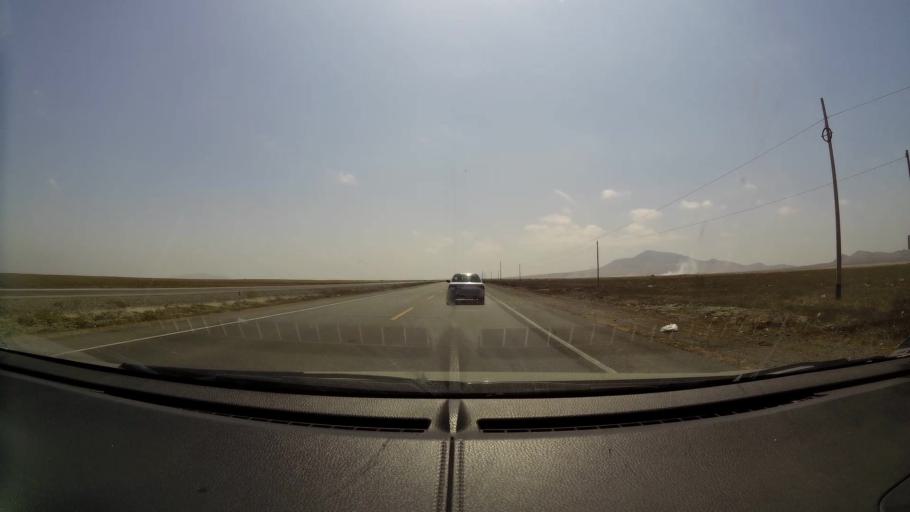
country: PE
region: Lambayeque
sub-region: Provincia de Chiclayo
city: Mocupe
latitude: -6.9398
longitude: -79.7218
